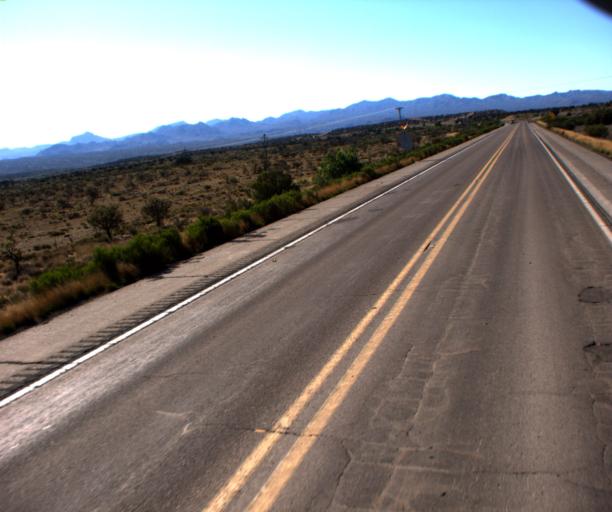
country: US
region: Arizona
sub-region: Mohave County
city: New Kingman-Butler
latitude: 35.1536
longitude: -113.6928
